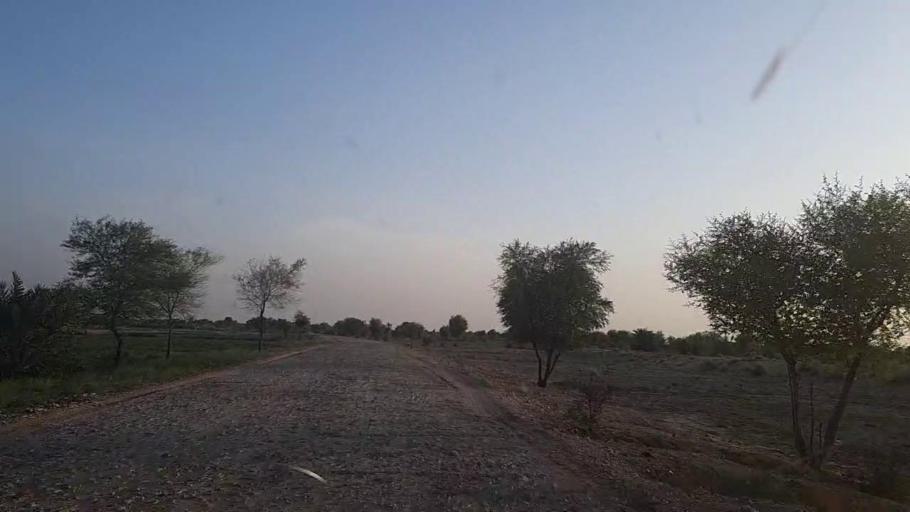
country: PK
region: Sindh
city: Khanpur
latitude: 27.6092
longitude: 69.4365
